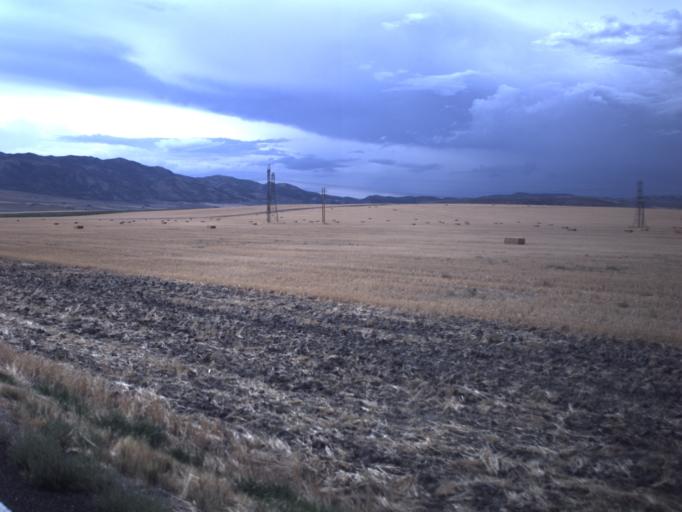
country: US
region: Utah
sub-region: Cache County
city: Benson
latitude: 41.9174
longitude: -111.9930
